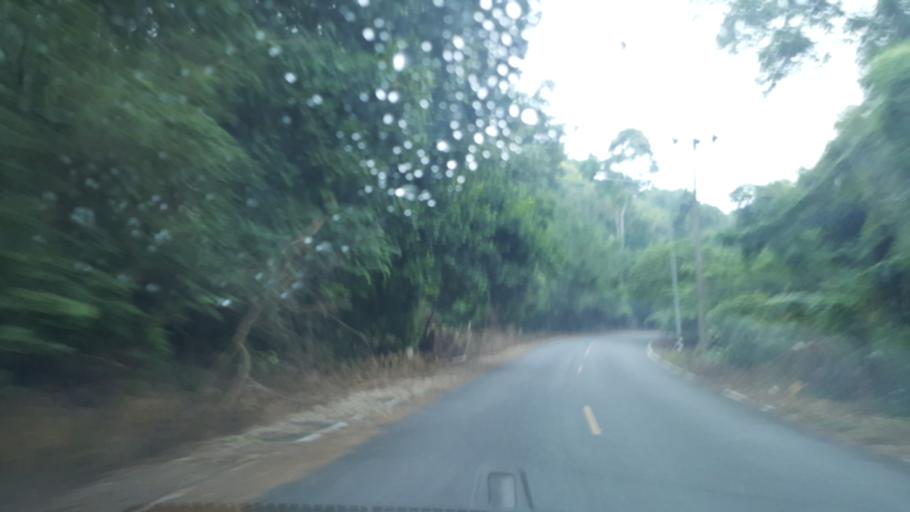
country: TH
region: Chon Buri
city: Ban Bueng
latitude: 13.2398
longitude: 101.0387
